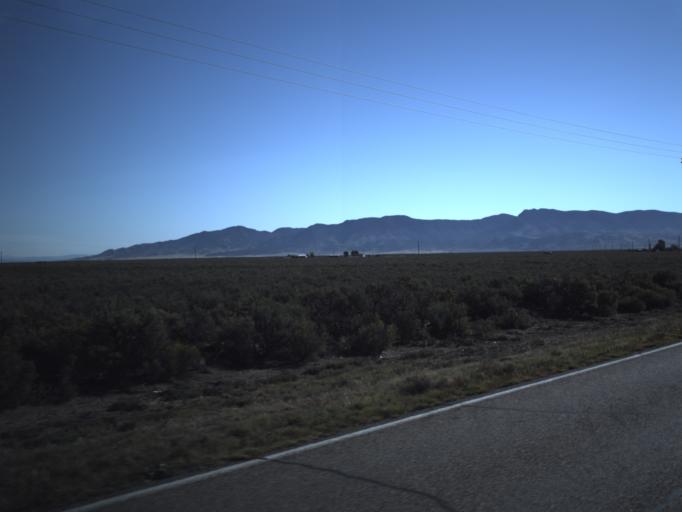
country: US
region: Utah
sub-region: Washington County
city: Enterprise
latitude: 37.7030
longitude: -113.6383
